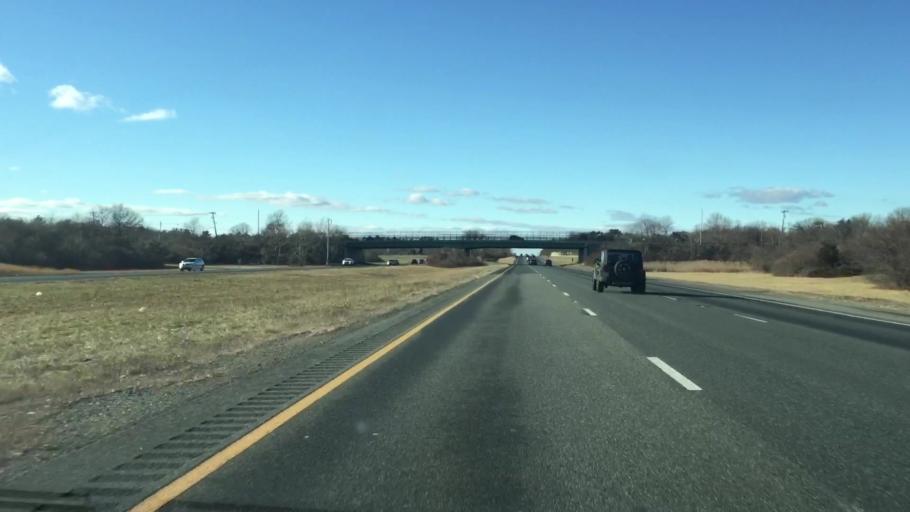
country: US
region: Massachusetts
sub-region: Bristol County
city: Raynham
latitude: 41.9590
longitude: -71.0658
